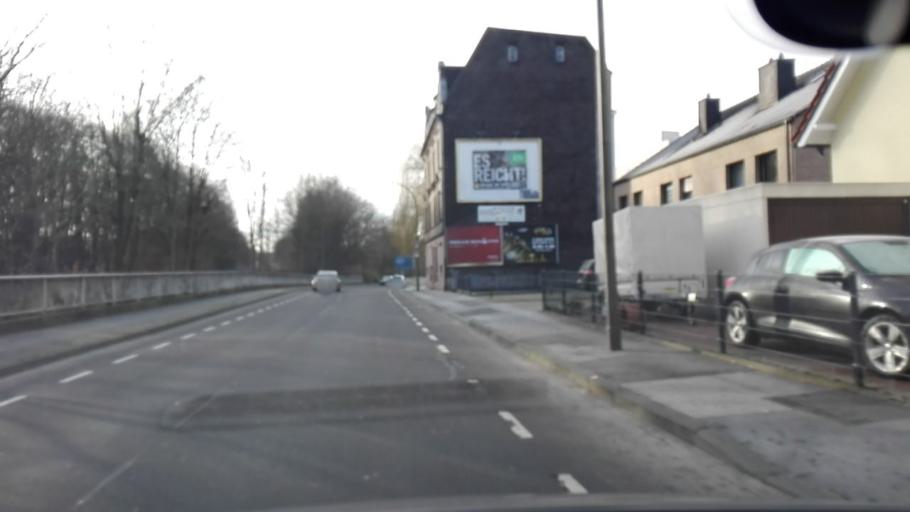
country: DE
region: North Rhine-Westphalia
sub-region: Regierungsbezirk Arnsberg
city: Dortmund
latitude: 51.5058
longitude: 7.4208
